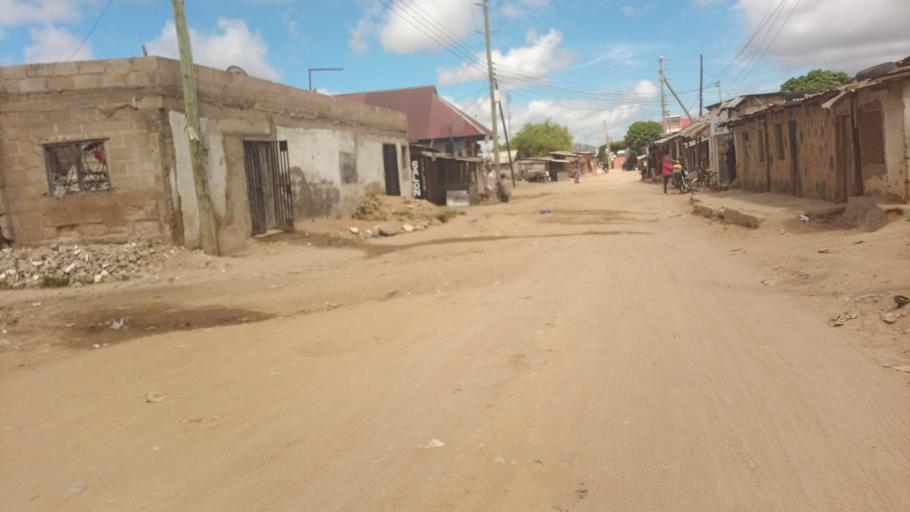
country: TZ
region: Dodoma
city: Kisasa
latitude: -6.1754
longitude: 35.7671
